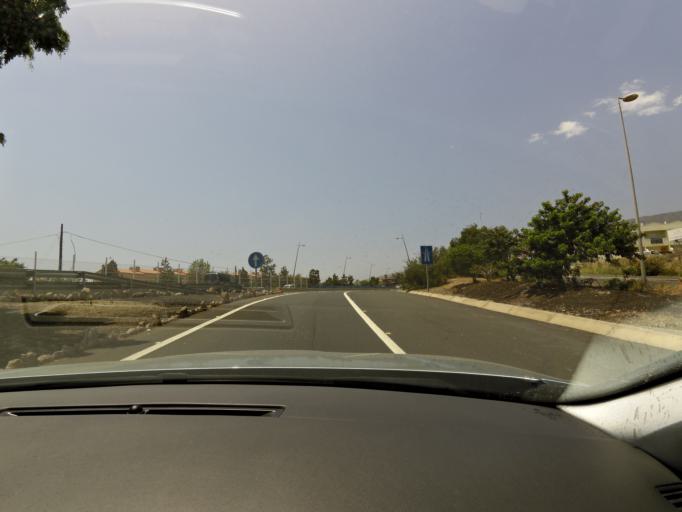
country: ES
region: Canary Islands
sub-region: Provincia de Santa Cruz de Tenerife
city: Playa de las Americas
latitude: 28.0903
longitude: -16.7289
